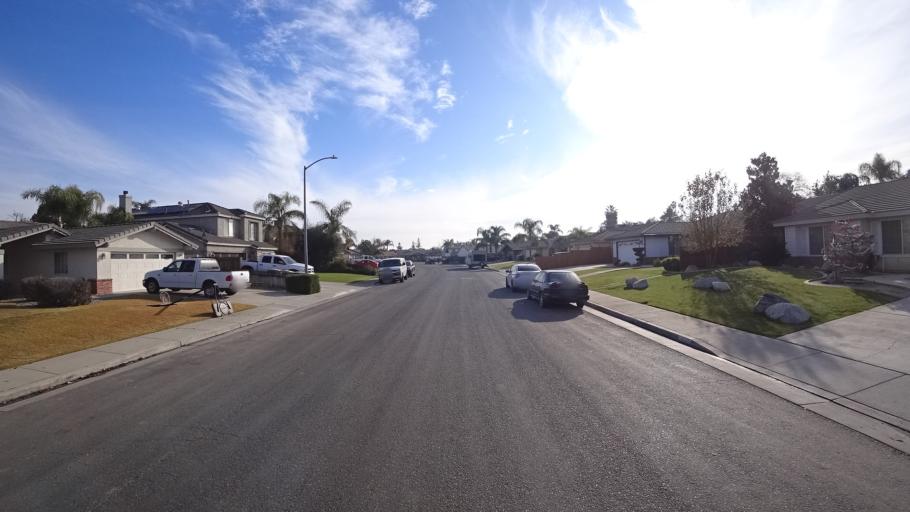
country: US
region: California
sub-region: Kern County
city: Rosedale
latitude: 35.4006
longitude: -119.1409
